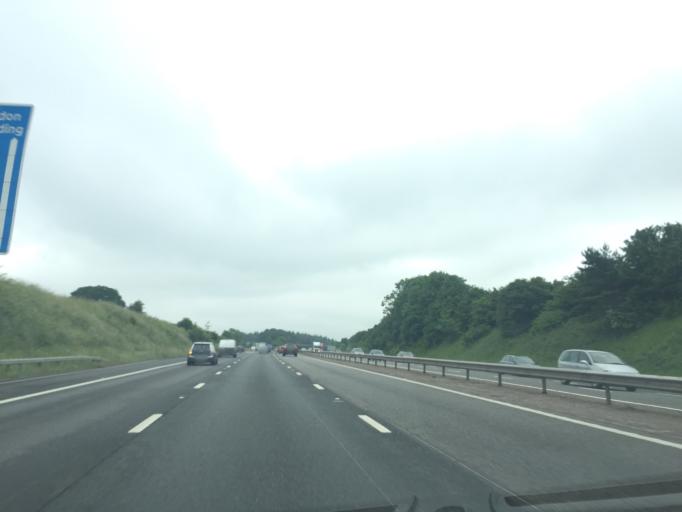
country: GB
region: England
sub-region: Hampshire
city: Basingstoke
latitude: 51.2155
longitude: -1.1670
